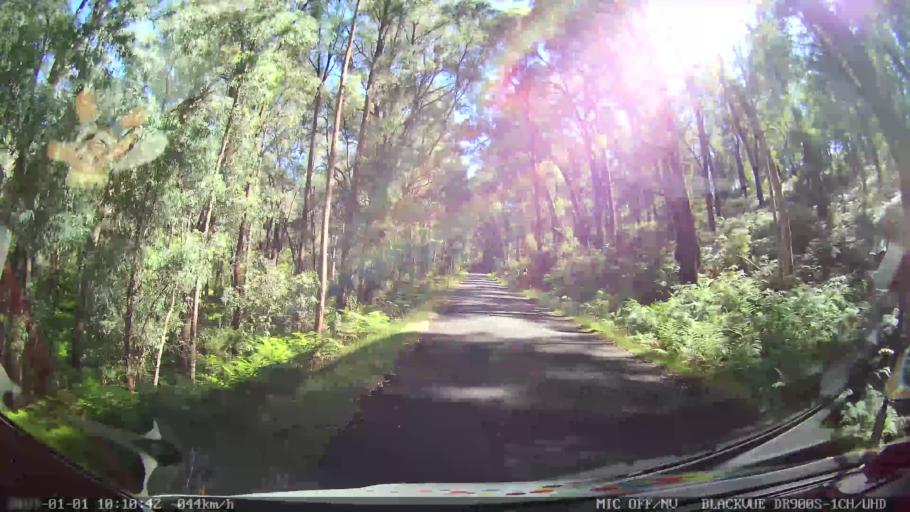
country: AU
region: New South Wales
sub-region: Snowy River
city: Jindabyne
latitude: -36.1395
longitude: 148.1580
